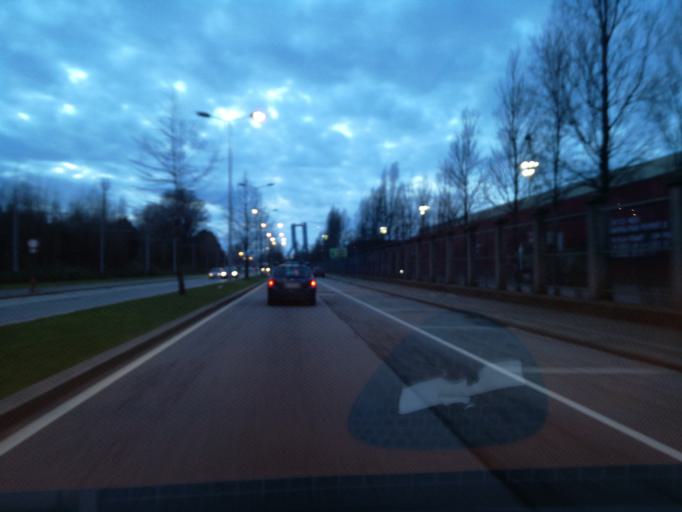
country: PT
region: Porto
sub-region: Matosinhos
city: Matosinhos
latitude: 41.1884
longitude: -8.6880
